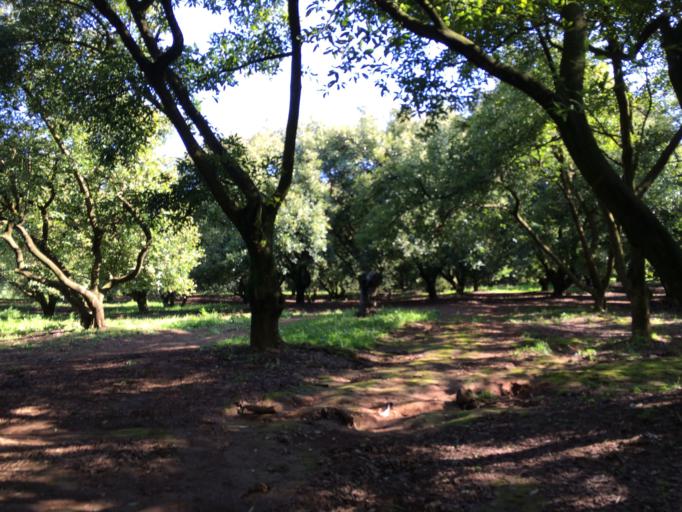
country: MX
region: Michoacan
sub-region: Uruapan
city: Nuevo Zirosto
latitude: 19.5570
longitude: -102.3510
